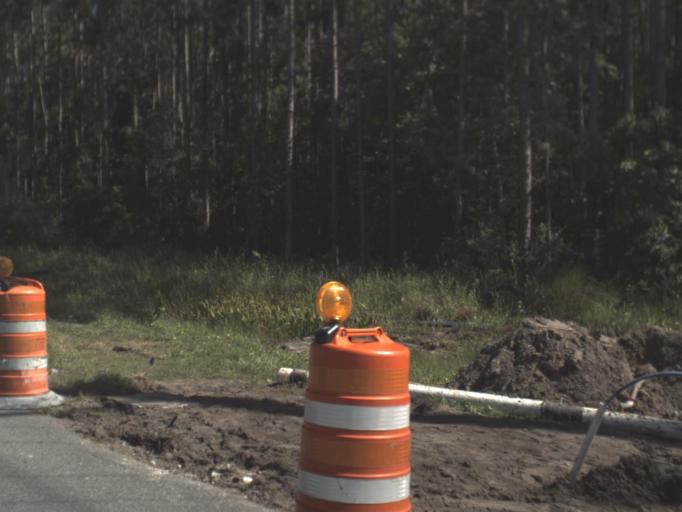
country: US
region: Florida
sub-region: Saint Johns County
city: Saint Augustine
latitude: 29.9371
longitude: -81.4360
